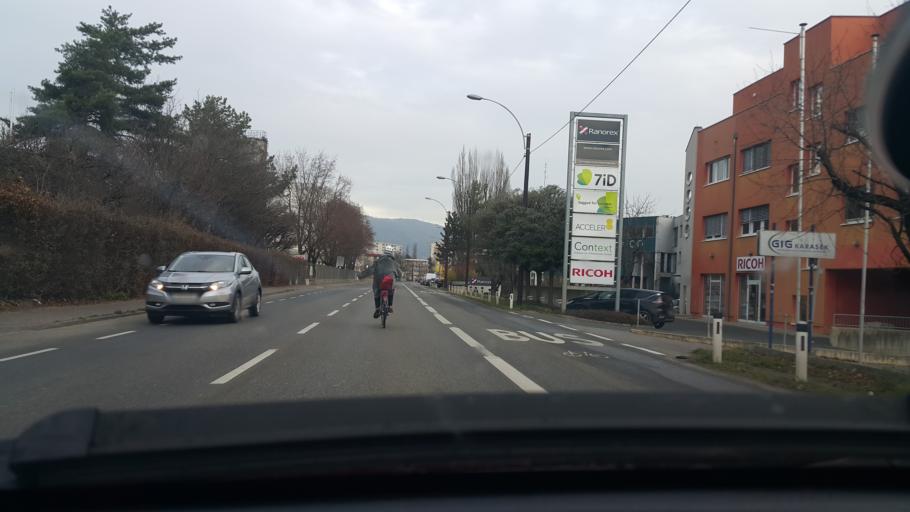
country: AT
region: Styria
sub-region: Graz Stadt
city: Wetzelsdorf
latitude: 47.0439
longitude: 15.3954
